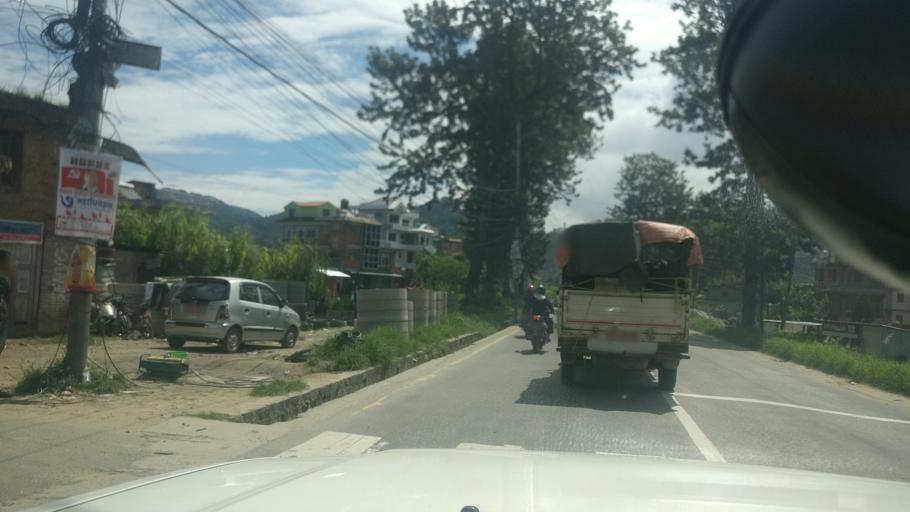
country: NP
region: Central Region
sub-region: Bagmati Zone
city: Hari Bdr Tamang House
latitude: 27.6535
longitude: 85.4597
